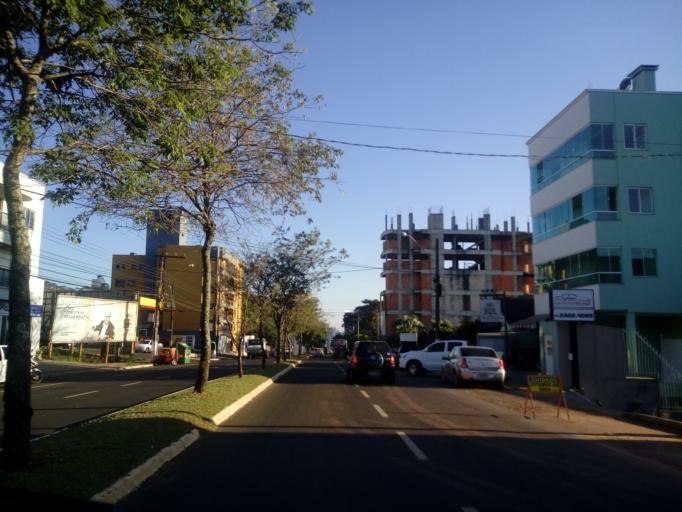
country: BR
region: Santa Catarina
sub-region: Chapeco
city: Chapeco
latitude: -27.1119
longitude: -52.6102
